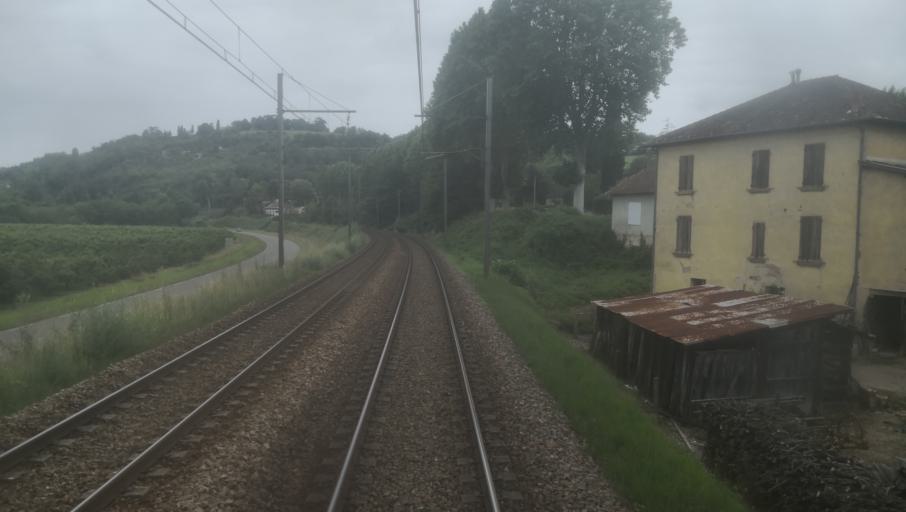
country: FR
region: Aquitaine
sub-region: Departement du Lot-et-Garonne
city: Port-Sainte-Marie
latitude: 44.2489
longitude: 0.4113
